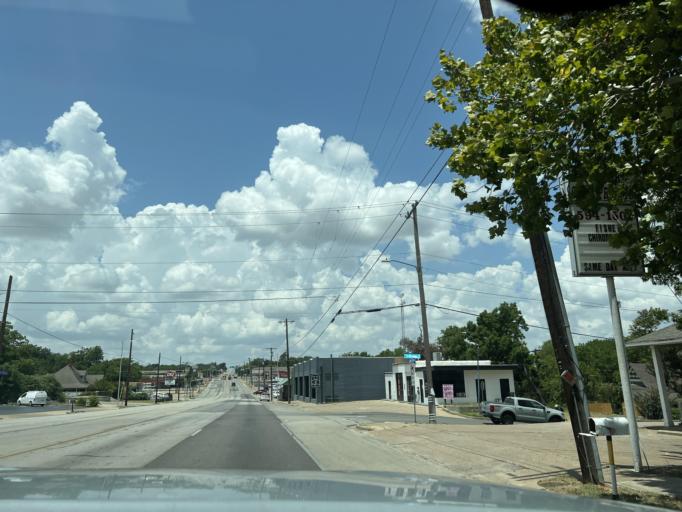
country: US
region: Texas
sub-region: Parker County
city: Weatherford
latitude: 32.7591
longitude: -97.8016
